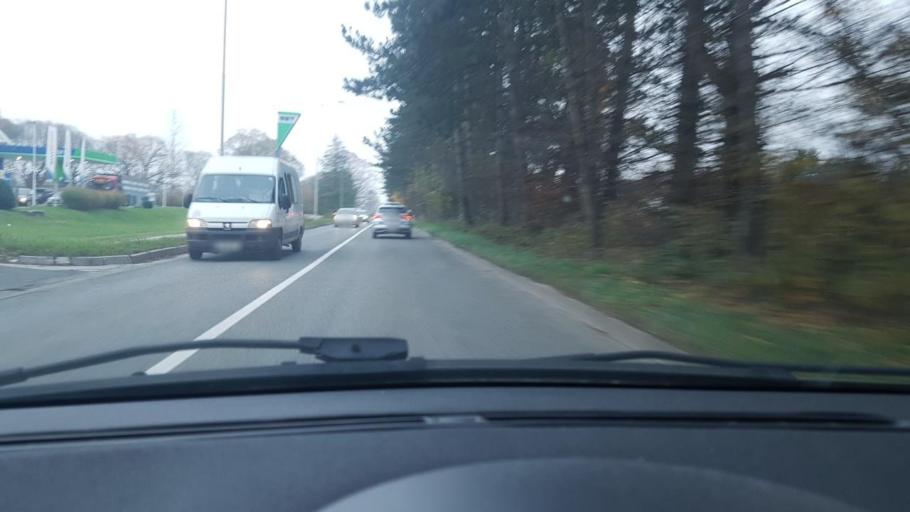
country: SI
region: Celje
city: Celje
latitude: 46.2378
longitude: 15.2343
